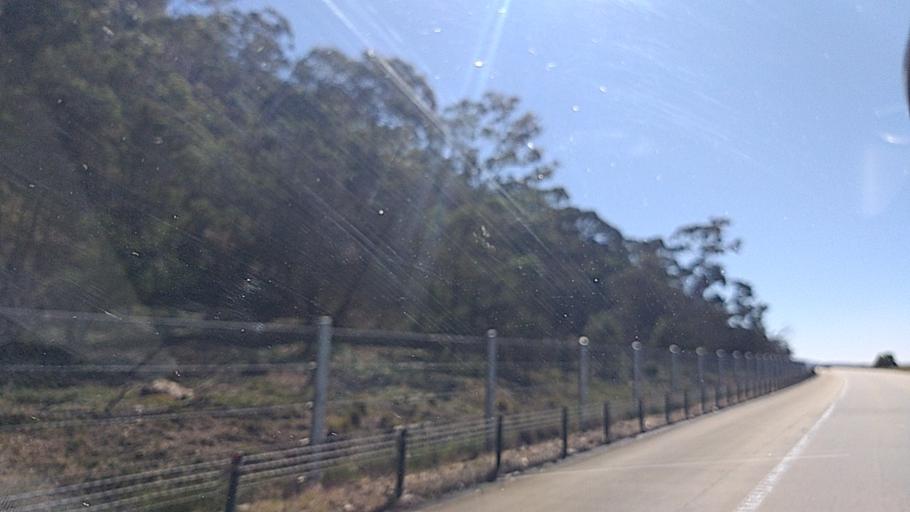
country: AU
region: New South Wales
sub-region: Yass Valley
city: Gundaroo
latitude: -35.0595
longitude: 149.3742
